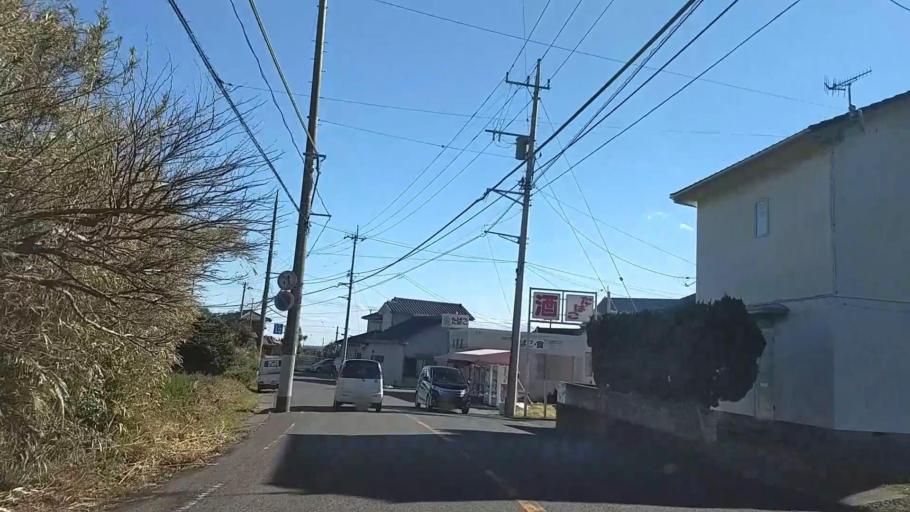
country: JP
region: Chiba
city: Tateyama
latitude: 34.9084
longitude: 139.9069
